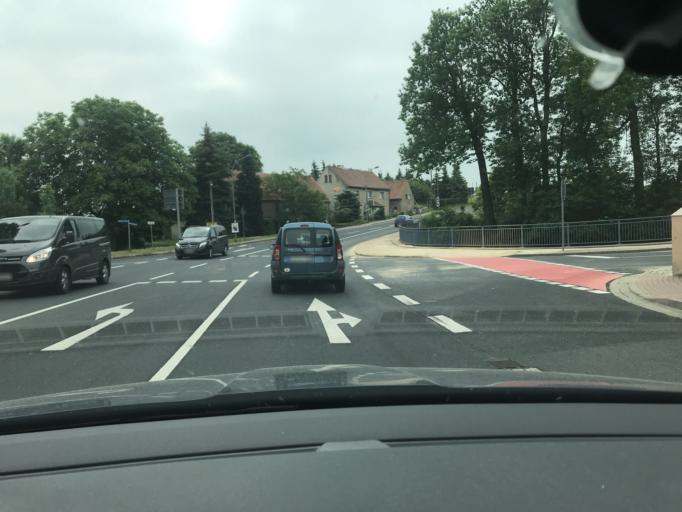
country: DE
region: Saxony
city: Priestewitz
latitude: 51.2283
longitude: 13.5051
